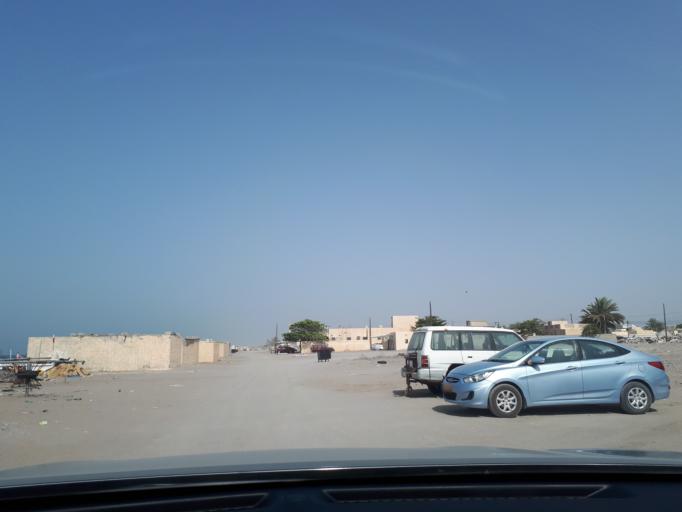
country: OM
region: Al Batinah
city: Barka'
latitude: 23.7077
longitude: 57.9305
